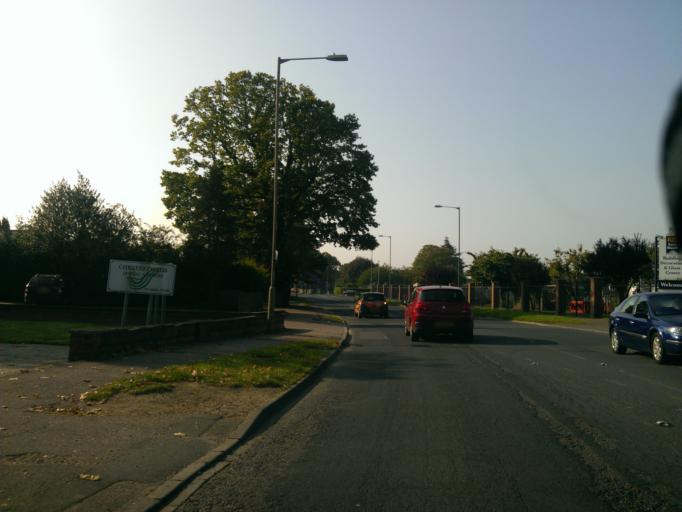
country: GB
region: England
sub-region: Essex
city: Layer de la Haye
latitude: 51.8661
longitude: 0.8730
